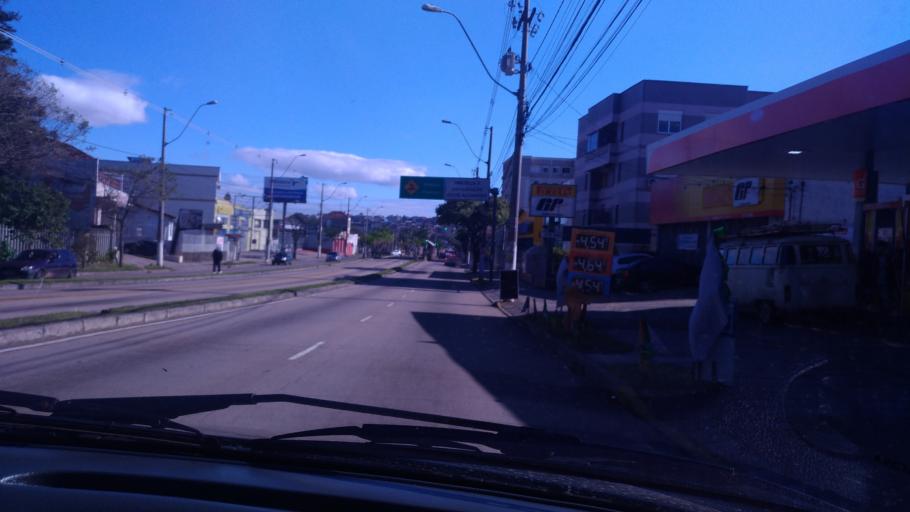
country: BR
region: Rio Grande do Sul
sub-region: Porto Alegre
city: Porto Alegre
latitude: -30.0729
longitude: -51.1977
